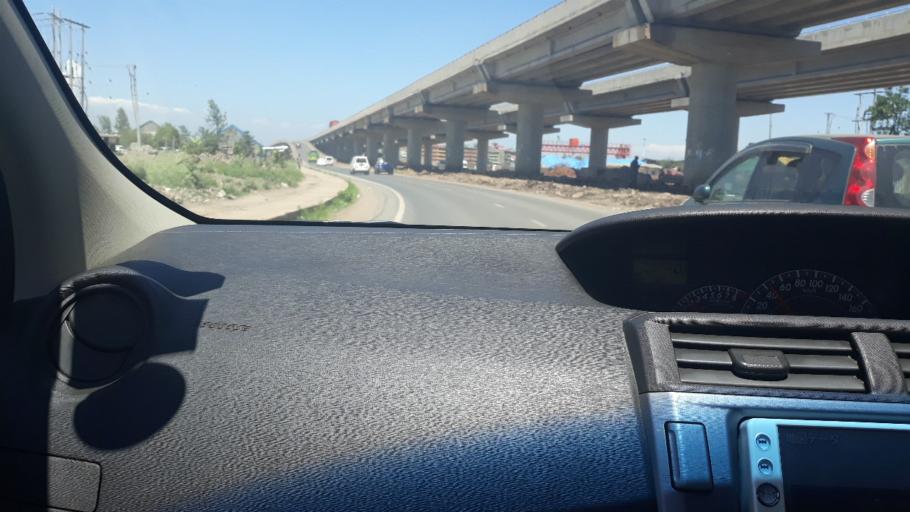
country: KE
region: Nairobi Area
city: Pumwani
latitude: -1.2783
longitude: 36.8825
